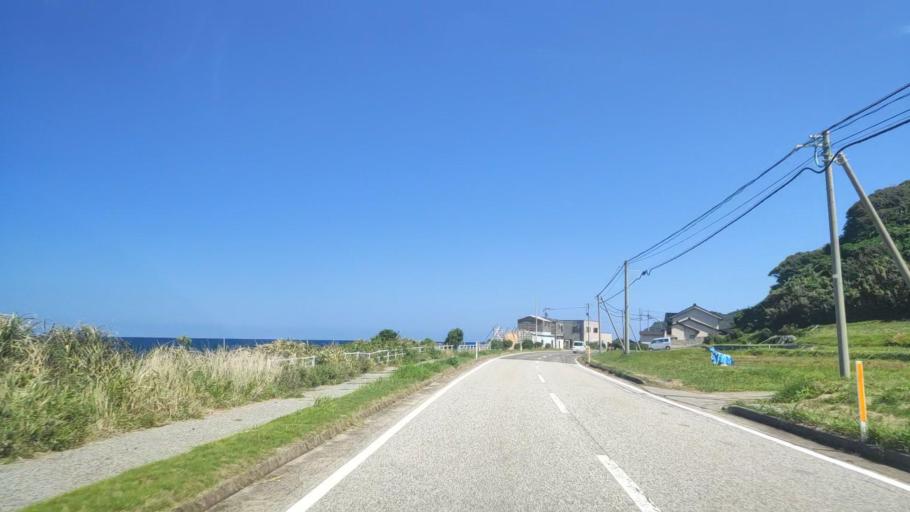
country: JP
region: Ishikawa
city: Nanao
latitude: 37.4926
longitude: 137.1262
